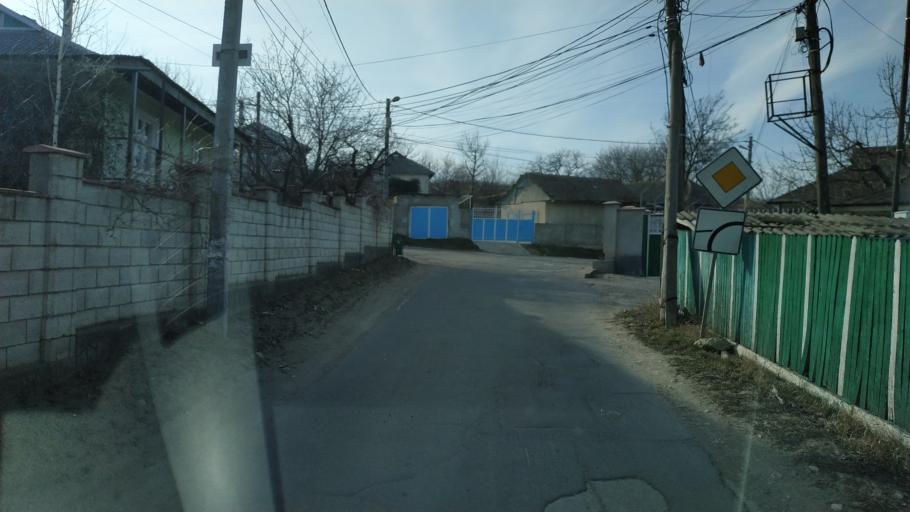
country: MD
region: Chisinau
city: Vatra
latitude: 47.0711
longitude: 28.6738
